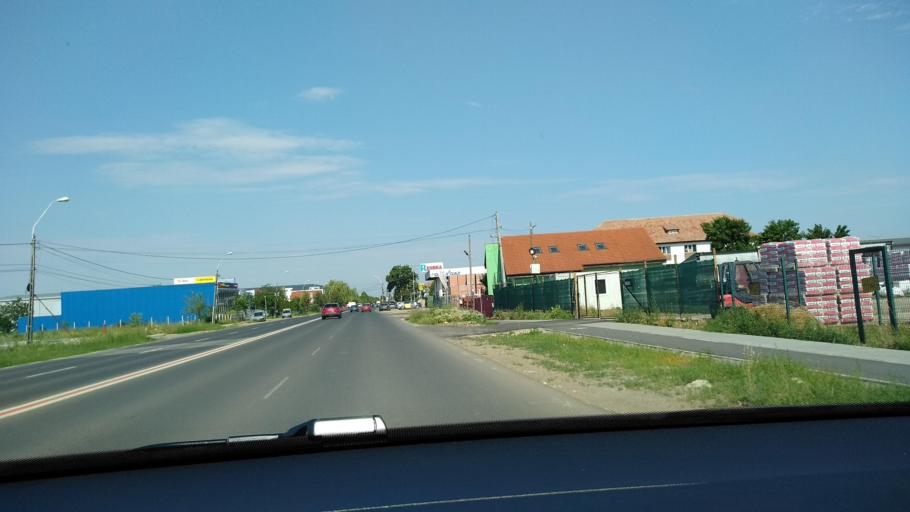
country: RO
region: Timis
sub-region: Comuna Ghiroda
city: Ghiroda
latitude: 45.7258
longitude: 21.2834
